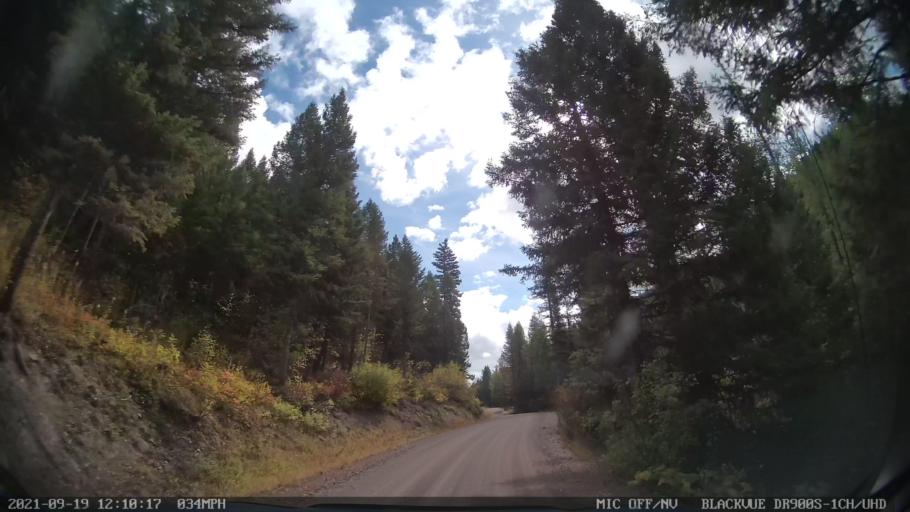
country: US
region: Montana
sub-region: Missoula County
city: Seeley Lake
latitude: 47.1798
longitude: -113.3847
